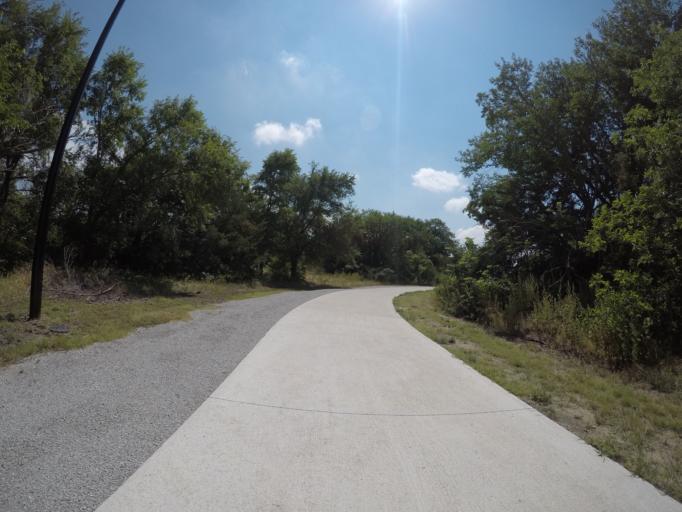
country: US
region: Nebraska
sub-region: Buffalo County
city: Kearney
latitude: 40.6726
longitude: -99.0306
